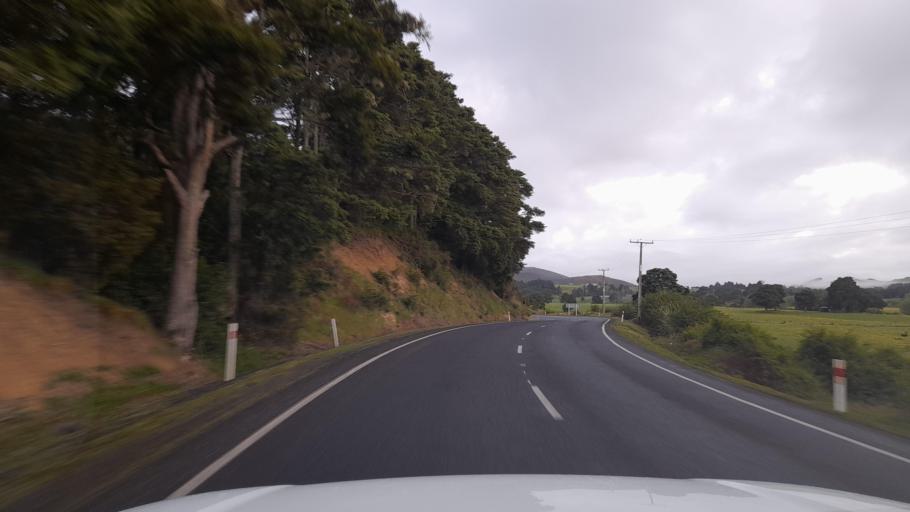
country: NZ
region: Northland
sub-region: Whangarei
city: Maungatapere
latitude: -35.7136
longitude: 174.0300
